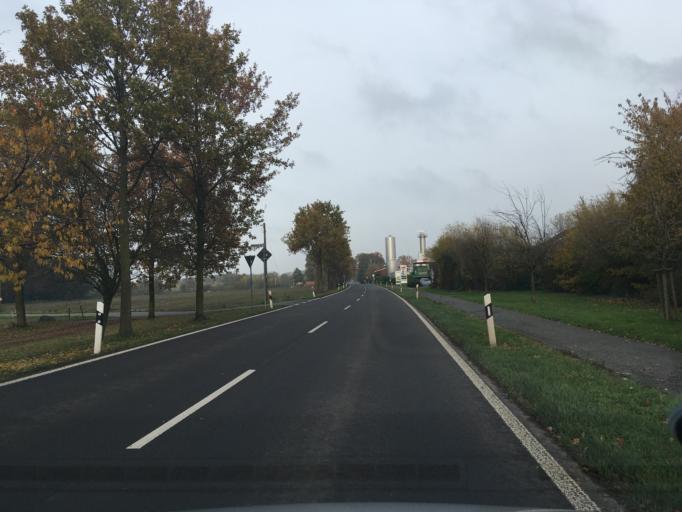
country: DE
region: North Rhine-Westphalia
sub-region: Regierungsbezirk Munster
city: Velen
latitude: 51.8960
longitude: 6.9736
